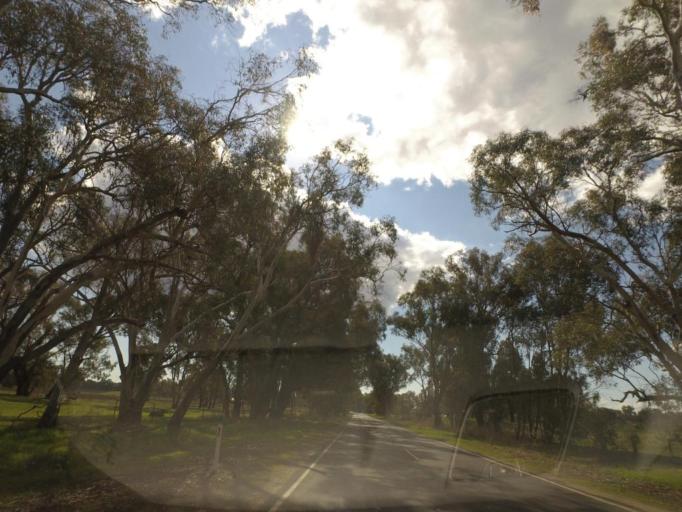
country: AU
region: New South Wales
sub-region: Corowa Shire
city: Howlong
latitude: -36.1708
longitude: 146.6079
